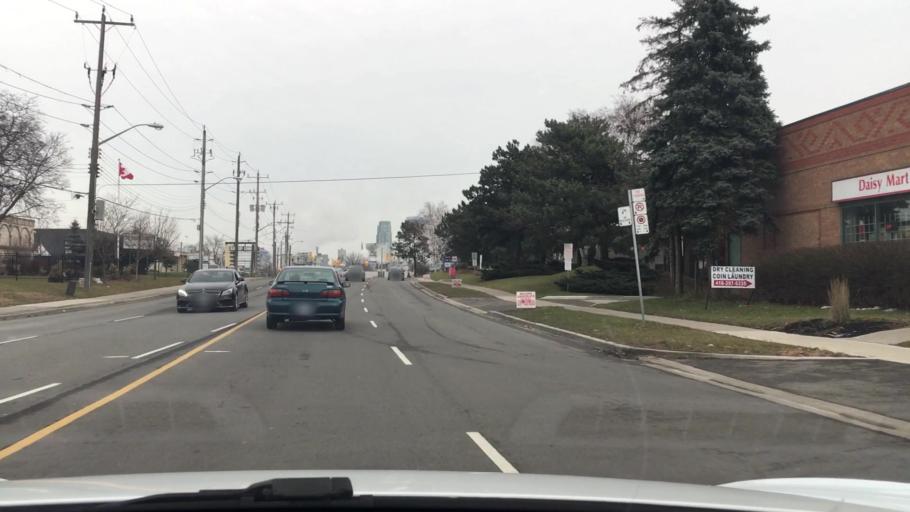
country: CA
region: Ontario
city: Scarborough
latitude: 43.7696
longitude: -79.2813
